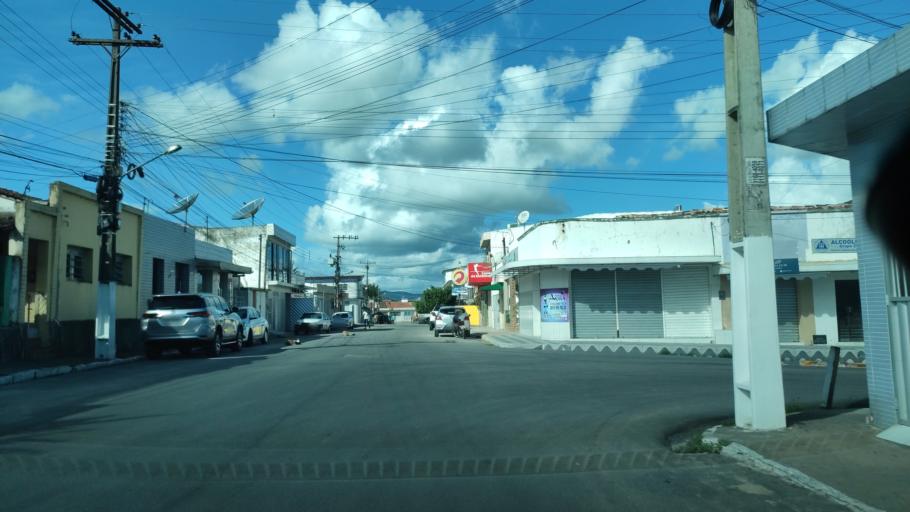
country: BR
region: Alagoas
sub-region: Uniao Dos Palmares
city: Uniao dos Palmares
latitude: -9.1554
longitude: -36.0309
